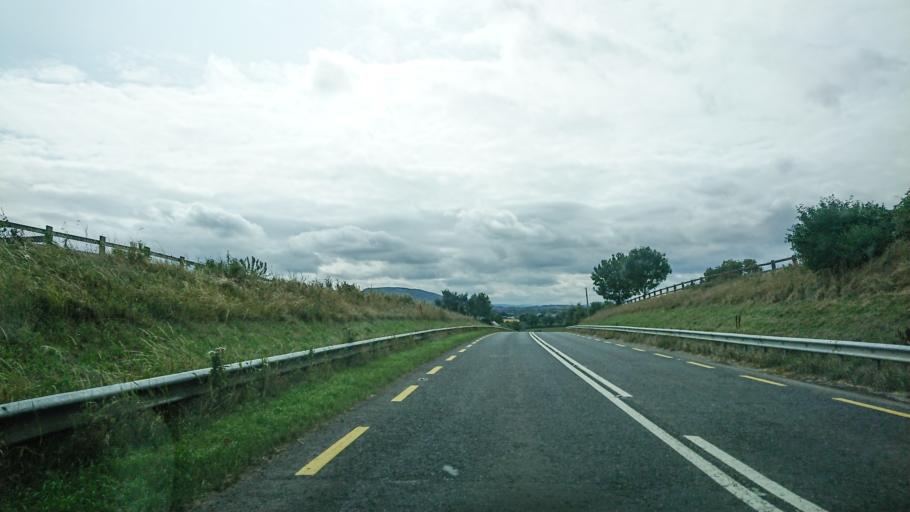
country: IE
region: Munster
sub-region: County Cork
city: Mallow
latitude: 52.1566
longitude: -8.4924
